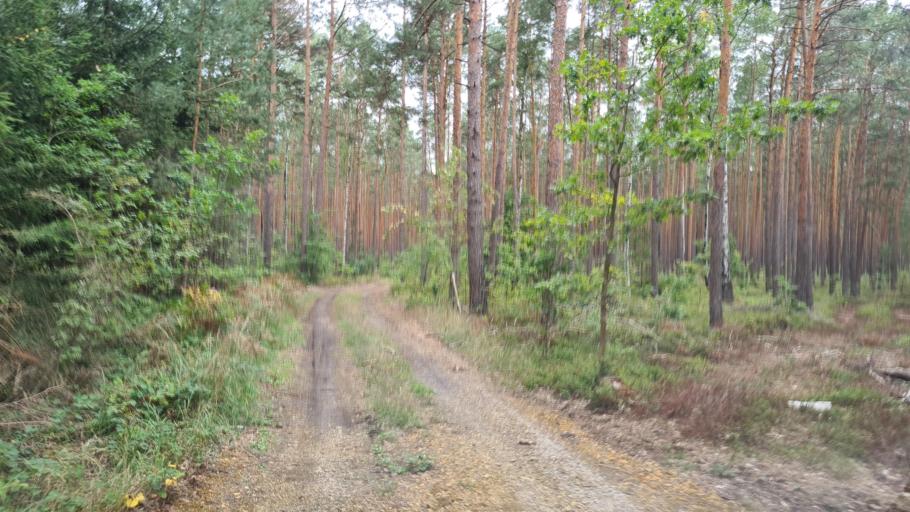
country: DE
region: Brandenburg
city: Schonborn
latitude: 51.6272
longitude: 13.5113
